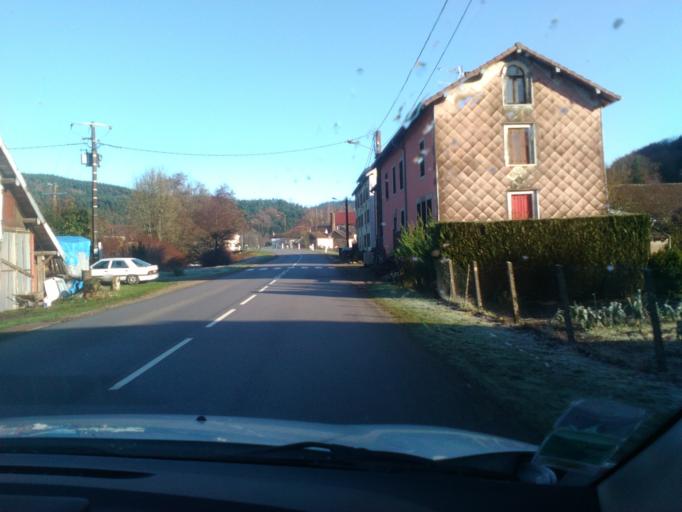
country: FR
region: Lorraine
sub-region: Departement des Vosges
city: Plombieres-les-Bains
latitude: 47.9365
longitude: 6.5045
